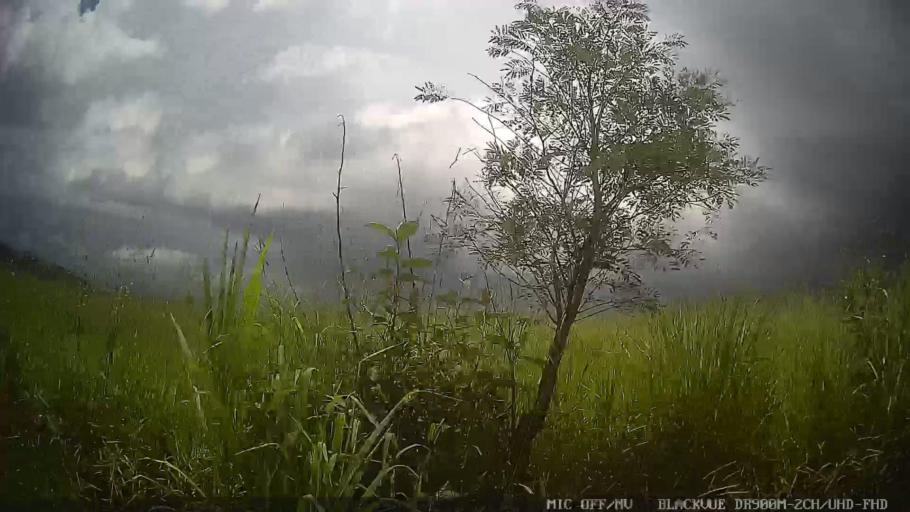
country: BR
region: Sao Paulo
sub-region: Atibaia
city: Atibaia
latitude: -23.1601
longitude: -46.5955
